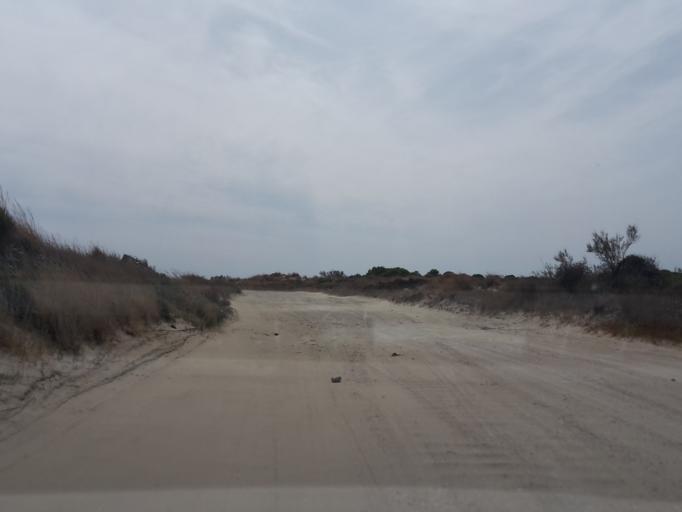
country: FR
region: Provence-Alpes-Cote d'Azur
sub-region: Departement des Bouches-du-Rhone
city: Saintes-Maries-de-la-Mer
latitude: 43.4128
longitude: 4.6106
